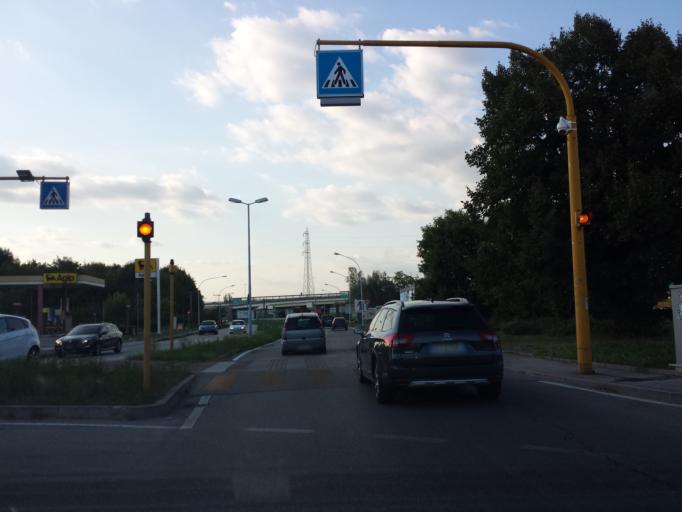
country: IT
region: Veneto
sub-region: Provincia di Padova
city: Mejaniga
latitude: 45.4349
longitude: 11.8972
